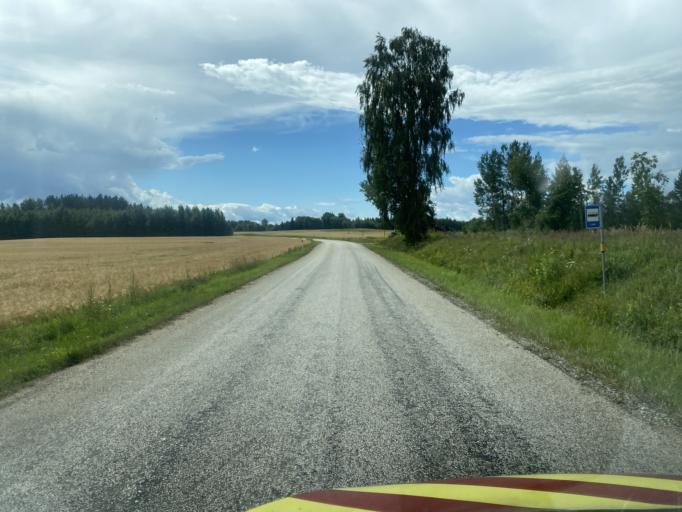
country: EE
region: Valgamaa
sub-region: Torva linn
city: Torva
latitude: 57.9560
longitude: 25.8854
